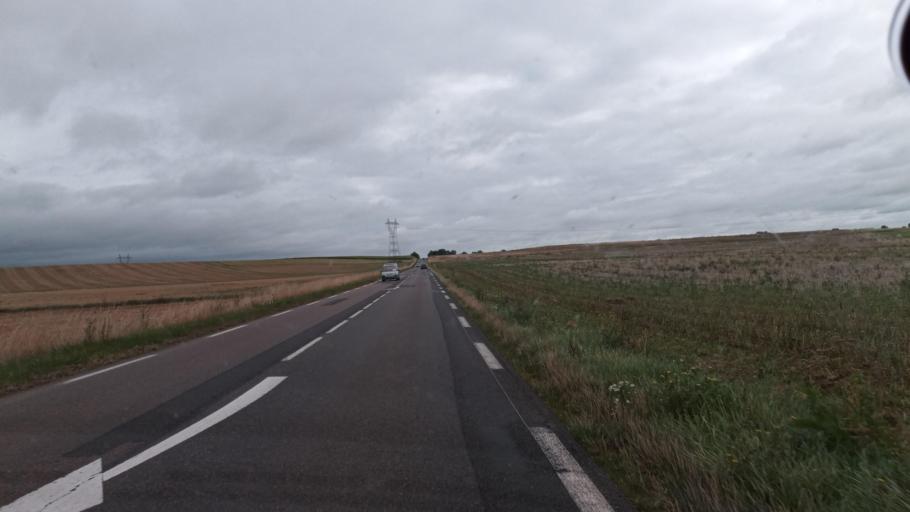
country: FR
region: Ile-de-France
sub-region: Departement de Seine-et-Marne
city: Voulx
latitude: 48.3264
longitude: 2.9545
